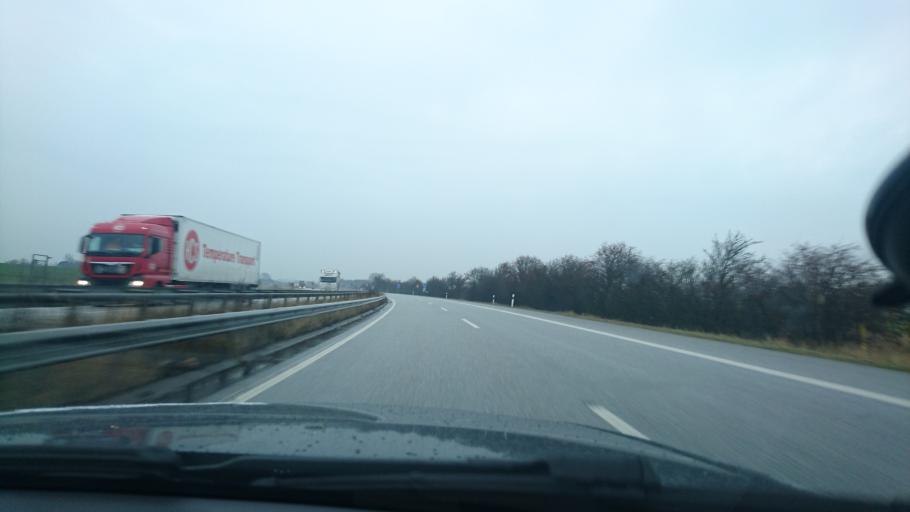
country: DE
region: Schleswig-Holstein
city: Gremersdorf
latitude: 54.3243
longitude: 10.9305
